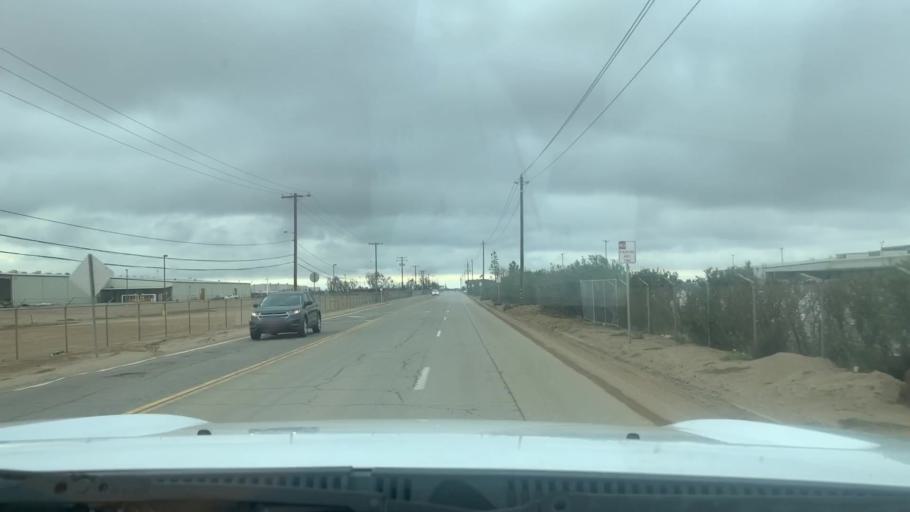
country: US
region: California
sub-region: Kern County
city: Shafter
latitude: 35.4952
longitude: -119.1630
